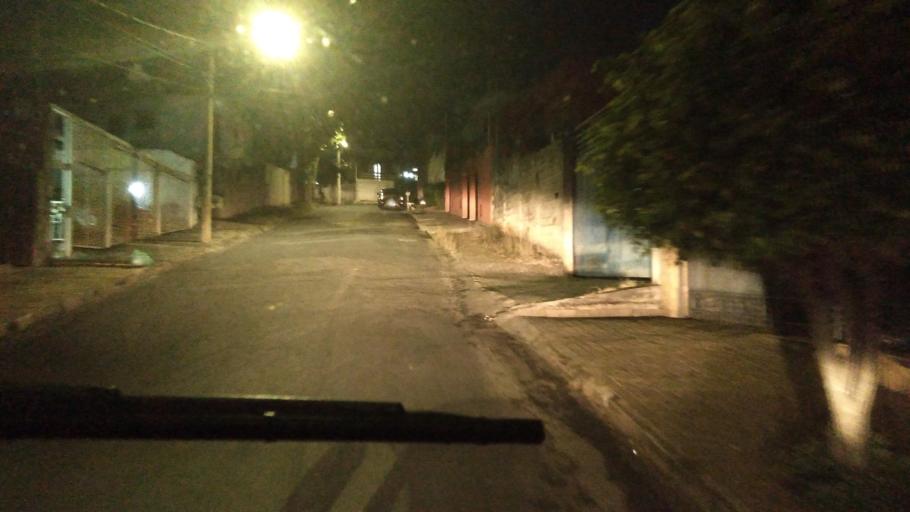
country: BR
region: Minas Gerais
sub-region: Belo Horizonte
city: Belo Horizonte
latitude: -19.8742
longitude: -43.9478
